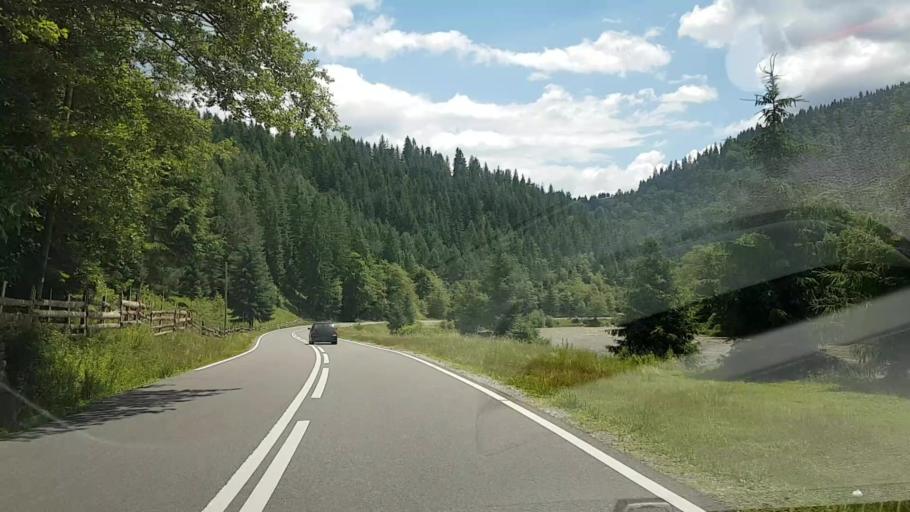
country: RO
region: Suceava
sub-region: Comuna Brosteni
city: Brosteni
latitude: 47.2629
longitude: 25.6659
